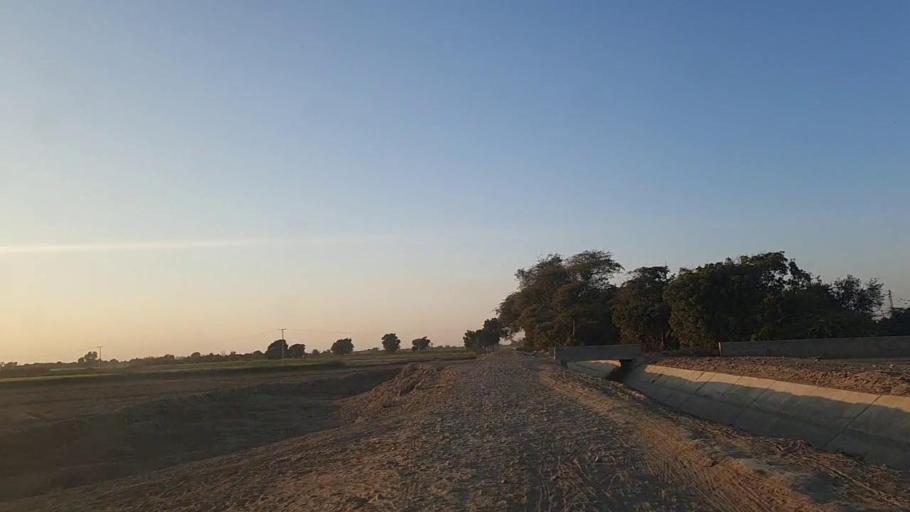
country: PK
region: Sindh
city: Naukot
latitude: 25.0372
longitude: 69.4101
